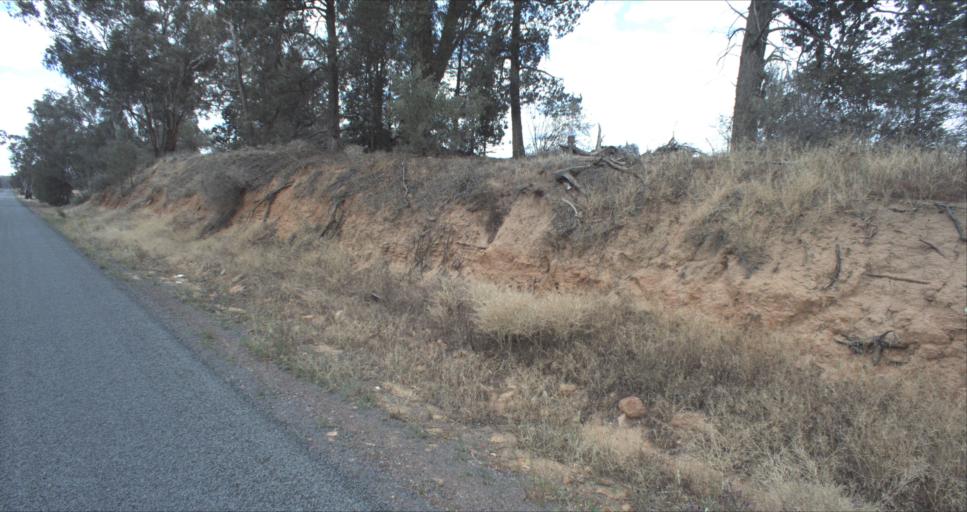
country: AU
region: New South Wales
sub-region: Leeton
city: Leeton
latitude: -34.6562
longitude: 146.3502
